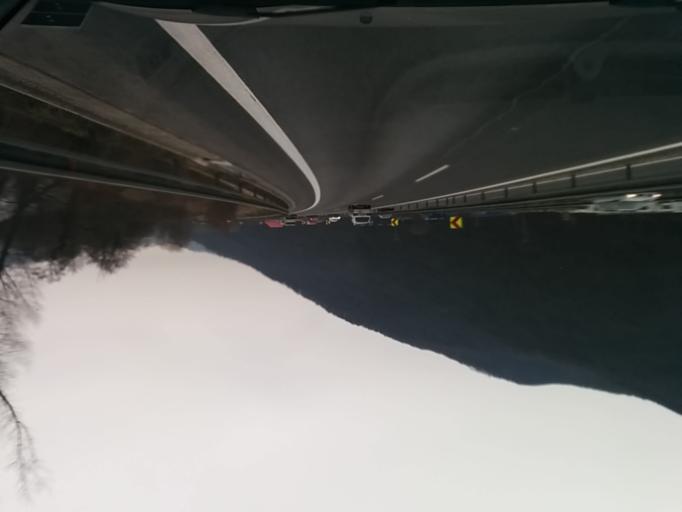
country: SK
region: Banskobystricky
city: Nova Bana
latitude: 48.4147
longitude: 18.6543
